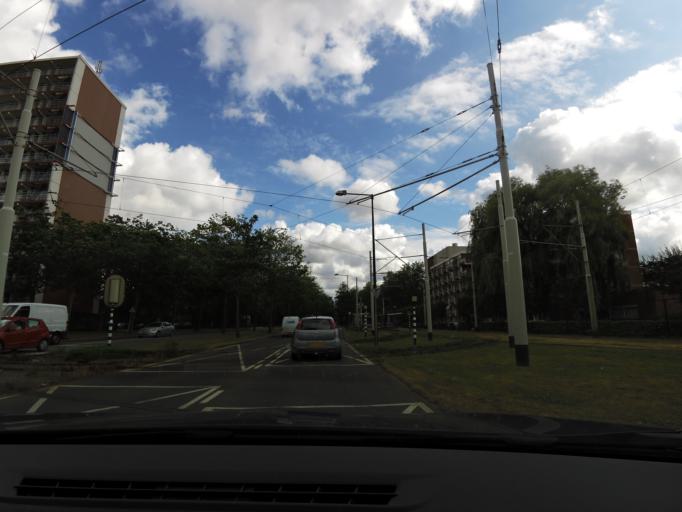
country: NL
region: South Holland
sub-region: Gemeente Vlaardingen
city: Vlaardingen
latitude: 51.9311
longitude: 4.3418
